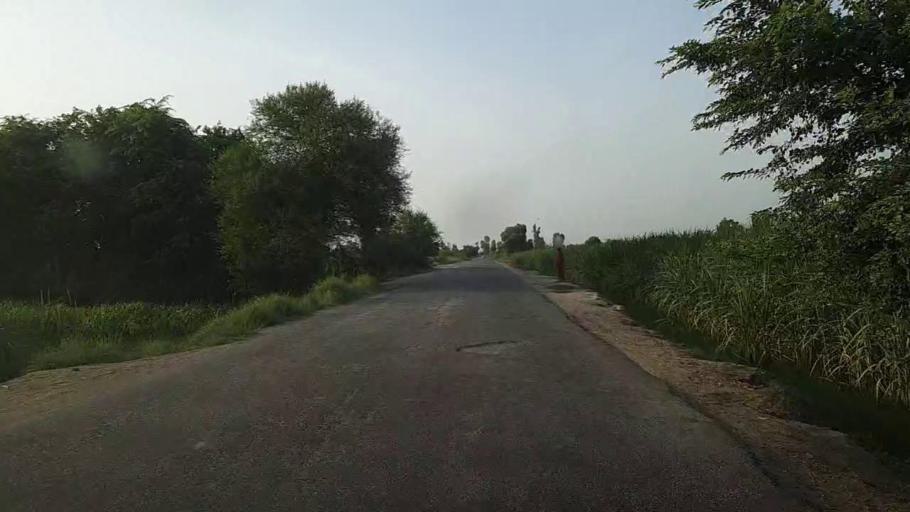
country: PK
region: Sindh
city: Ubauro
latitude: 28.1833
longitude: 69.8283
